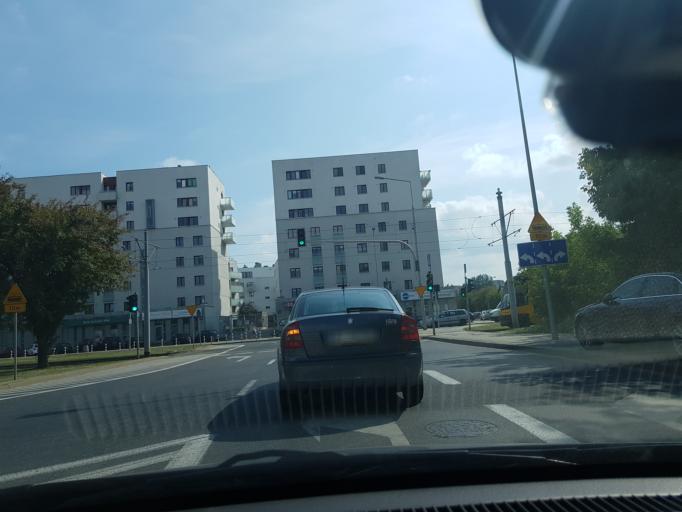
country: PL
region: Masovian Voivodeship
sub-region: Warszawa
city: Bielany
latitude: 52.2896
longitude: 20.9282
